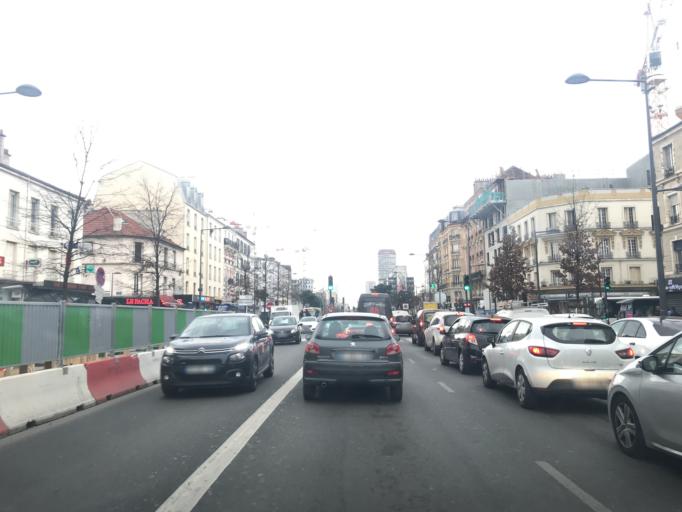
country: FR
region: Ile-de-France
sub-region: Departement du Val-de-Marne
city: Le Kremlin-Bicetre
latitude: 48.8142
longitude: 2.3611
